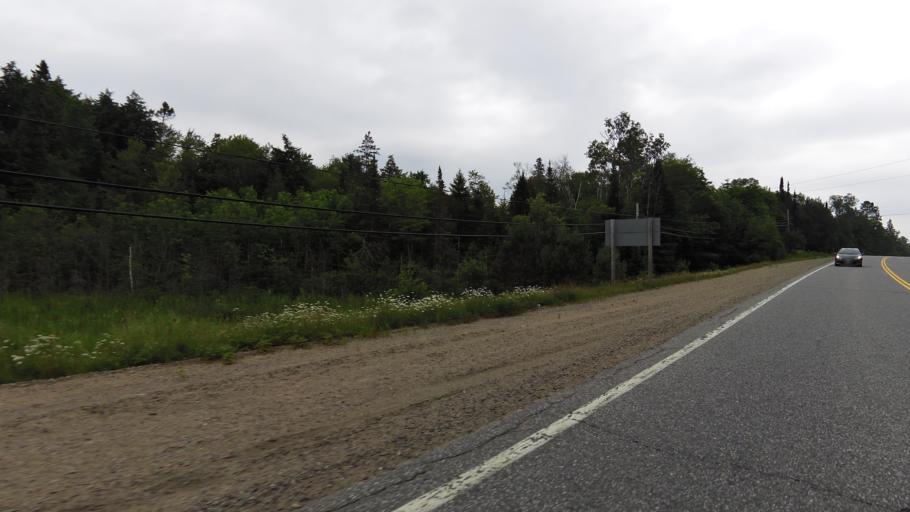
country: CA
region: Ontario
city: Huntsville
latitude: 45.3297
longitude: -79.0046
